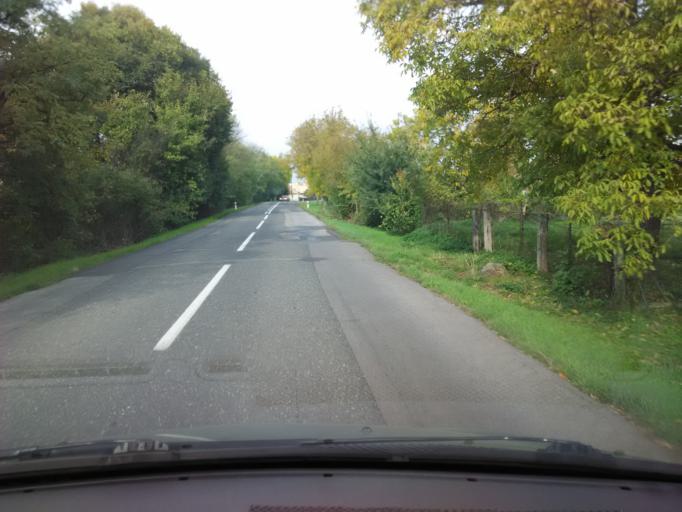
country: SK
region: Nitriansky
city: Tlmace
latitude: 48.2376
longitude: 18.5200
